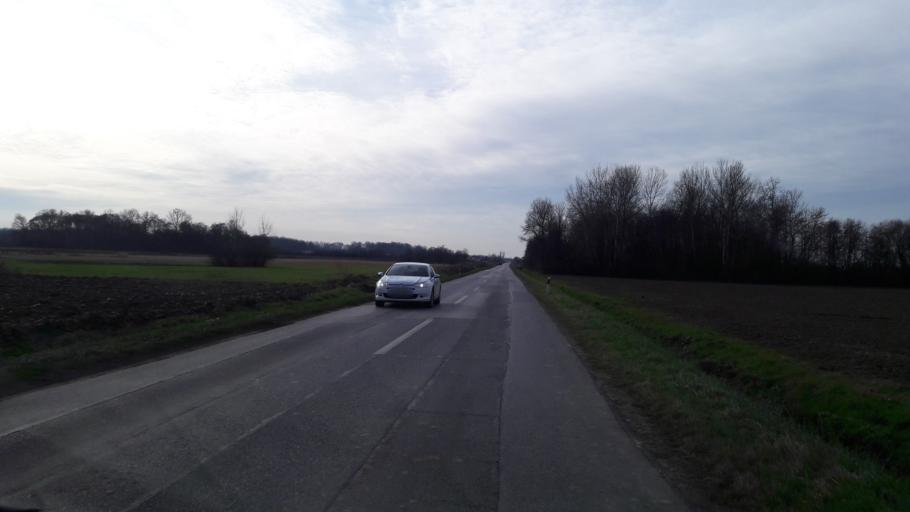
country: HR
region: Osjecko-Baranjska
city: Viskovci
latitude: 45.2878
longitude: 18.4655
